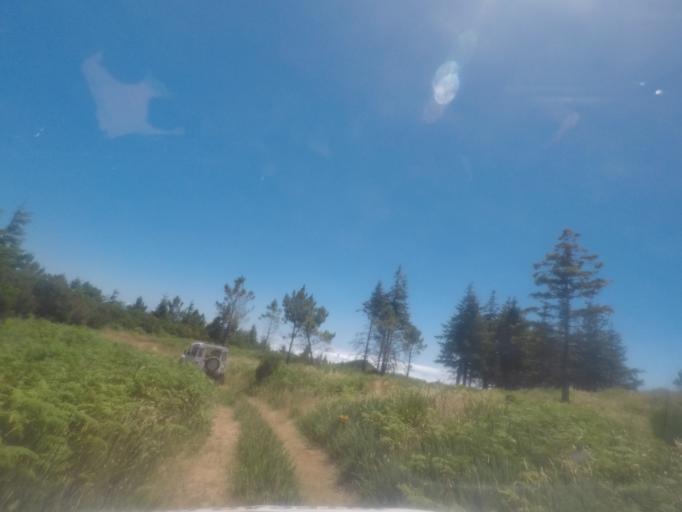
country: PT
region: Madeira
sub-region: Funchal
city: Nossa Senhora do Monte
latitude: 32.7102
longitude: -16.8979
